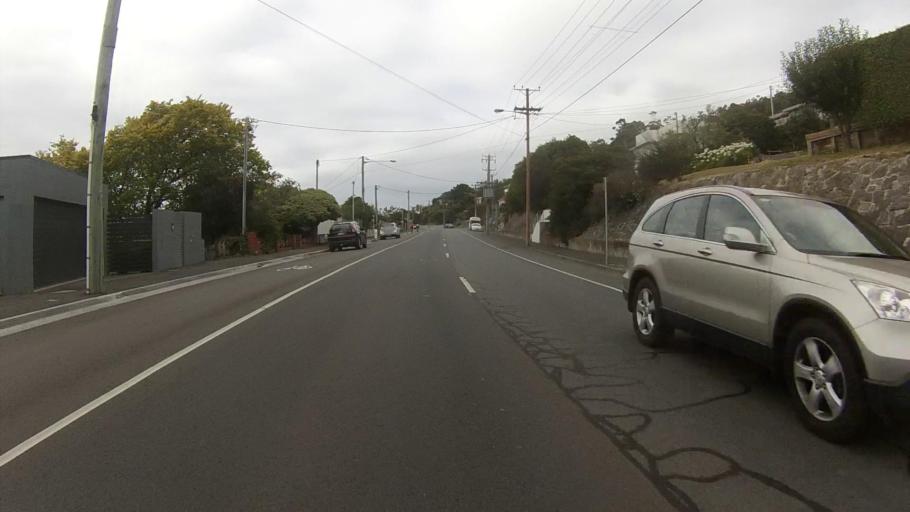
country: AU
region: Tasmania
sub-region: Kingborough
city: Taroona
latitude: -42.9198
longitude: 147.3601
